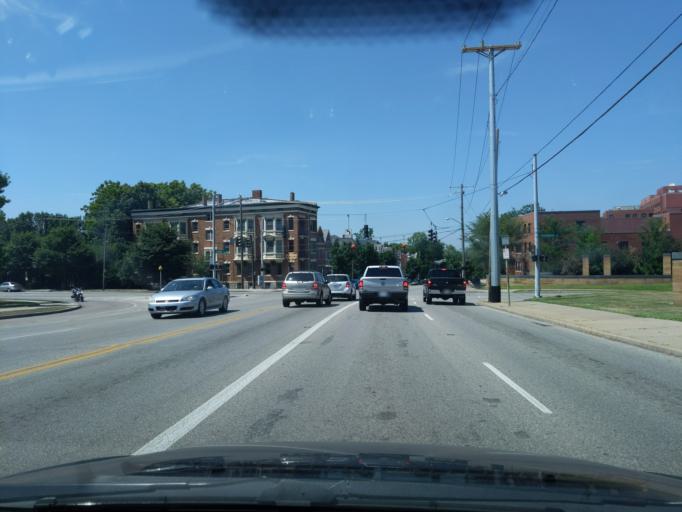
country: US
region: Ohio
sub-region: Hamilton County
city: Saint Bernard
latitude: 39.1373
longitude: -84.5093
